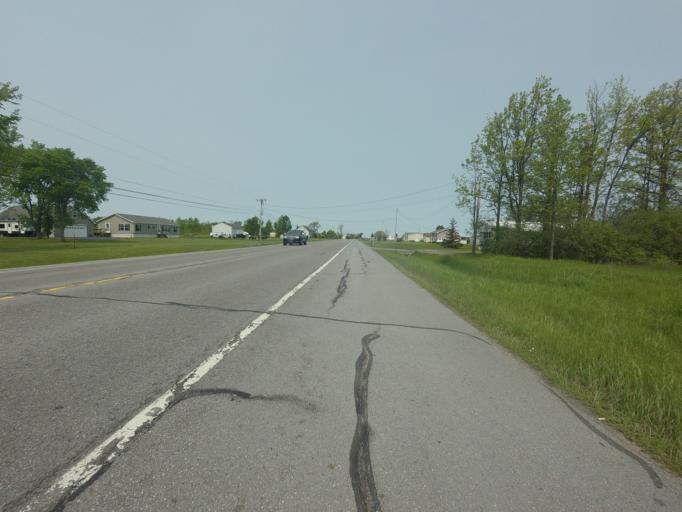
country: US
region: New York
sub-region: Jefferson County
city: Dexter
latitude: 44.0406
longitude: -76.0776
